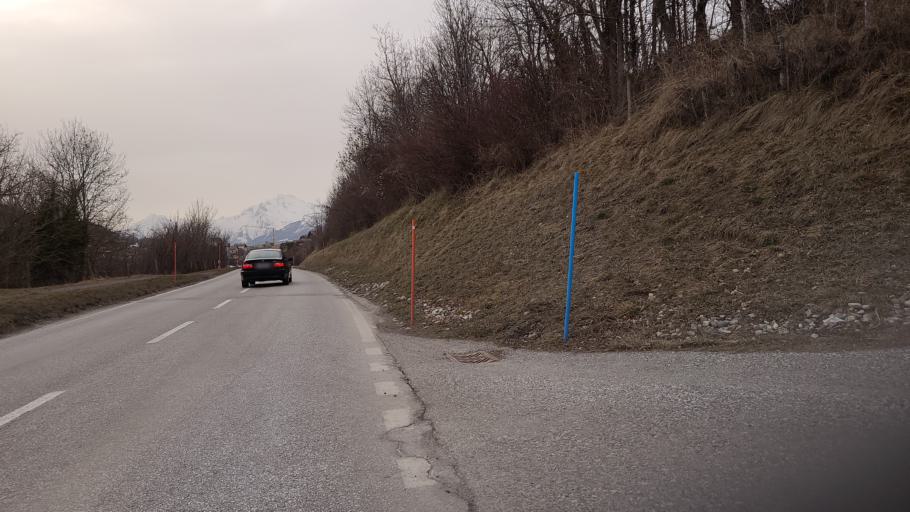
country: CH
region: Valais
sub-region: Sierre District
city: Lens
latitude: 46.2825
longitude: 7.4582
